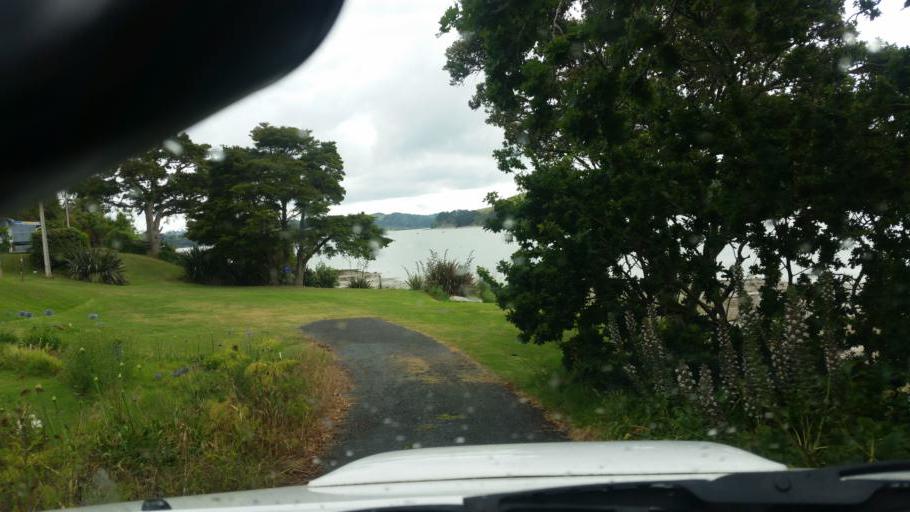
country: NZ
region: Auckland
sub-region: Auckland
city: Wellsford
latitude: -36.1548
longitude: 174.2279
